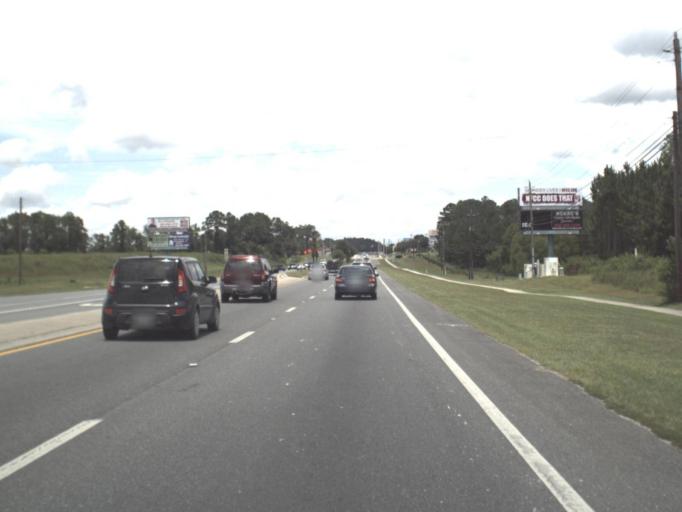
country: US
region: Florida
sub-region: Suwannee County
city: Live Oak
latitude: 30.3189
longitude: -82.9700
